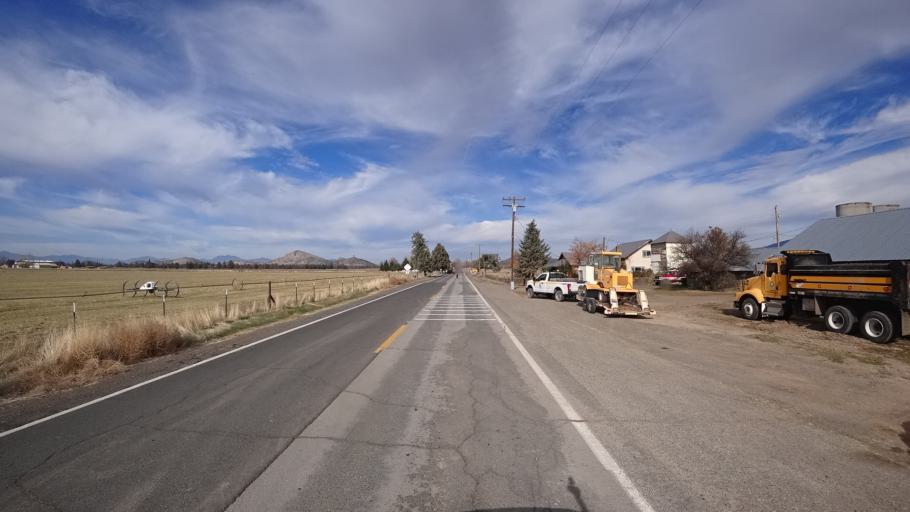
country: US
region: California
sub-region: Siskiyou County
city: Montague
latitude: 41.6218
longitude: -122.3996
